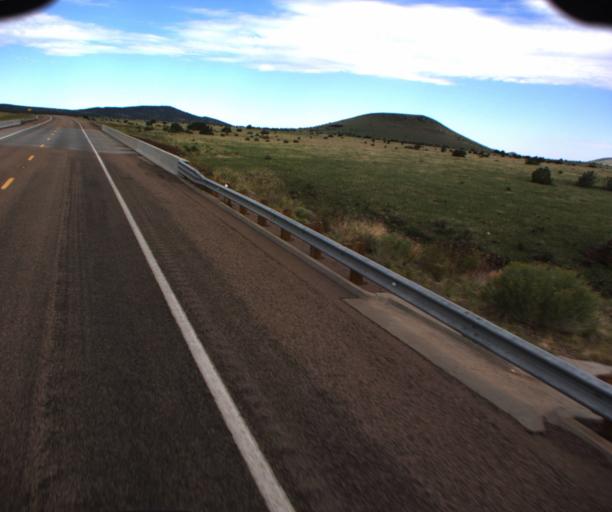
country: US
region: Arizona
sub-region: Apache County
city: Springerville
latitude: 34.2424
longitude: -109.5171
